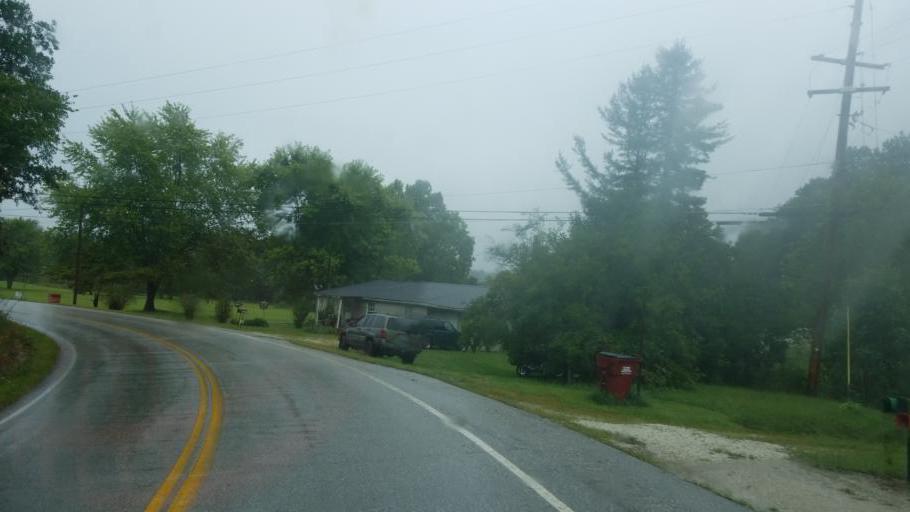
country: US
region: Ohio
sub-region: Scioto County
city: Franklin Furnace
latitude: 38.6456
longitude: -82.9258
